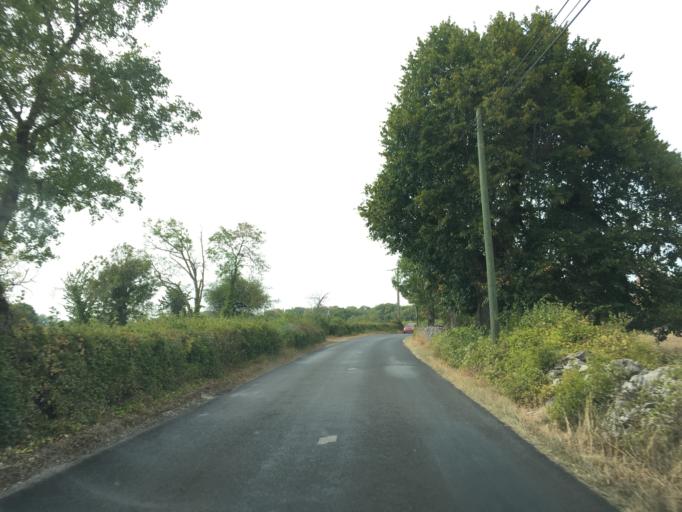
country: FR
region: Midi-Pyrenees
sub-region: Departement du Lot
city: Gramat
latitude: 44.8131
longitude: 1.6036
